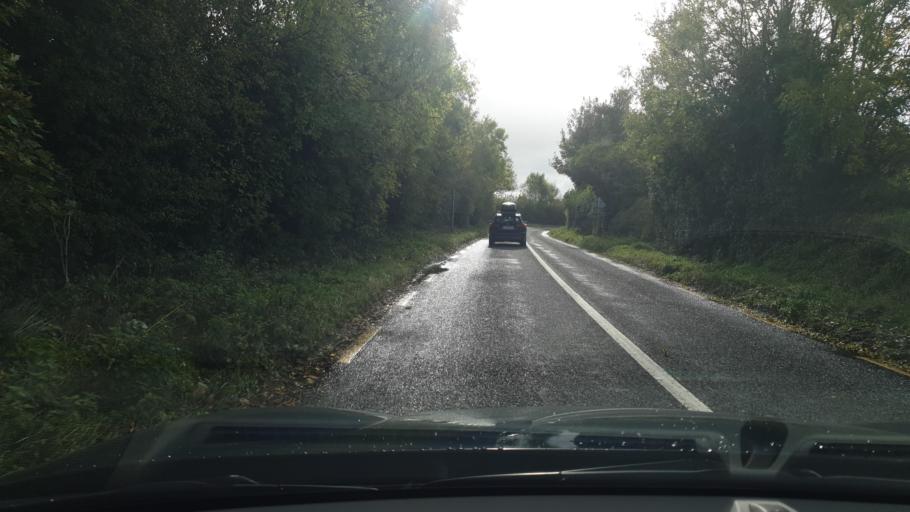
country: IE
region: Leinster
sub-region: An Mhi
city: Dunshaughlin
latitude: 53.5201
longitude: -6.5299
